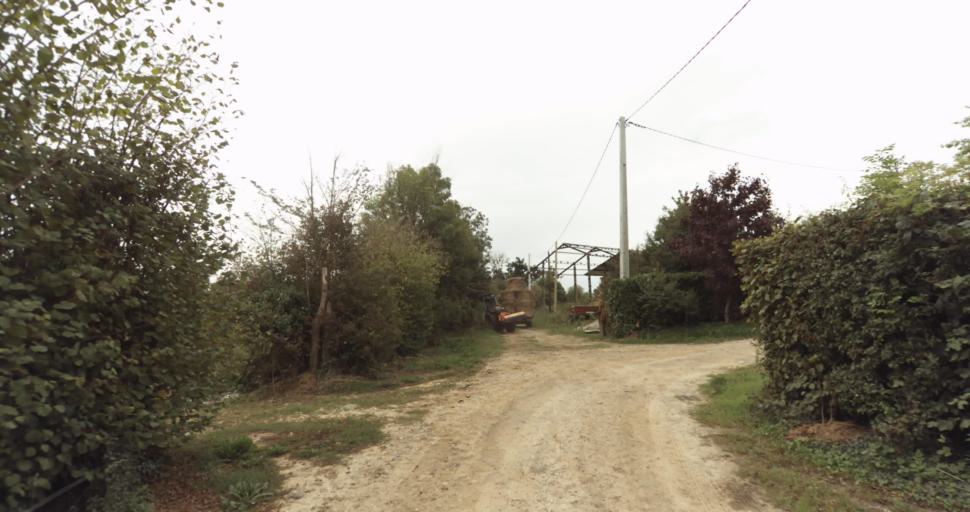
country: FR
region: Lower Normandy
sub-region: Departement de l'Orne
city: Gace
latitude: 48.7283
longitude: 0.2831
